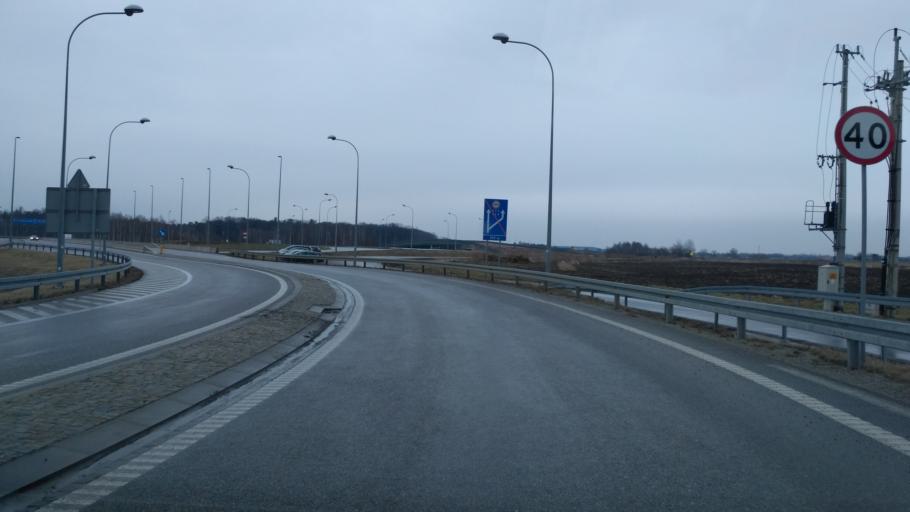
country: PL
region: Subcarpathian Voivodeship
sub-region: Powiat debicki
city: Brzeznica
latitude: 50.0752
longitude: 21.4686
